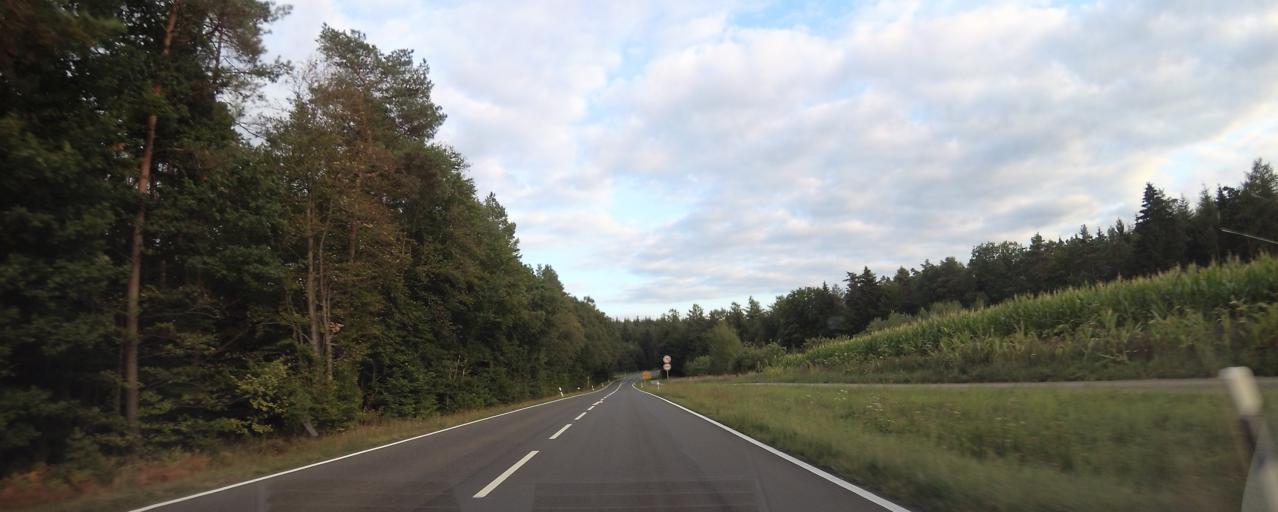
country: DE
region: Rheinland-Pfalz
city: Zemmer
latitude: 49.8872
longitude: 6.7149
